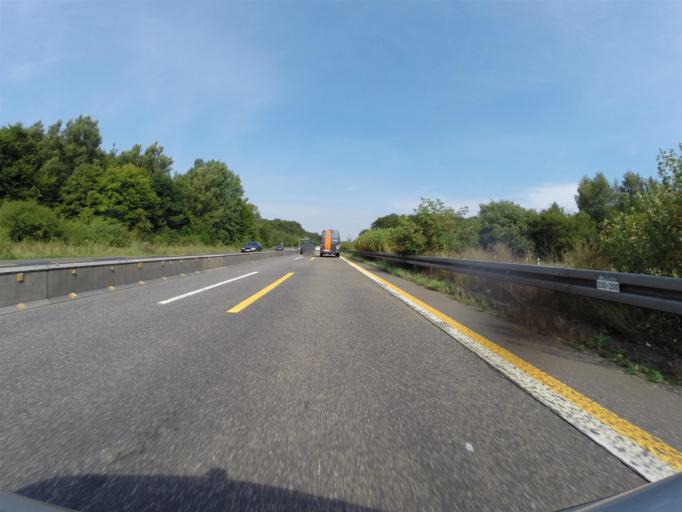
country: DE
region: Hesse
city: Felsberg
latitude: 51.1324
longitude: 9.4738
